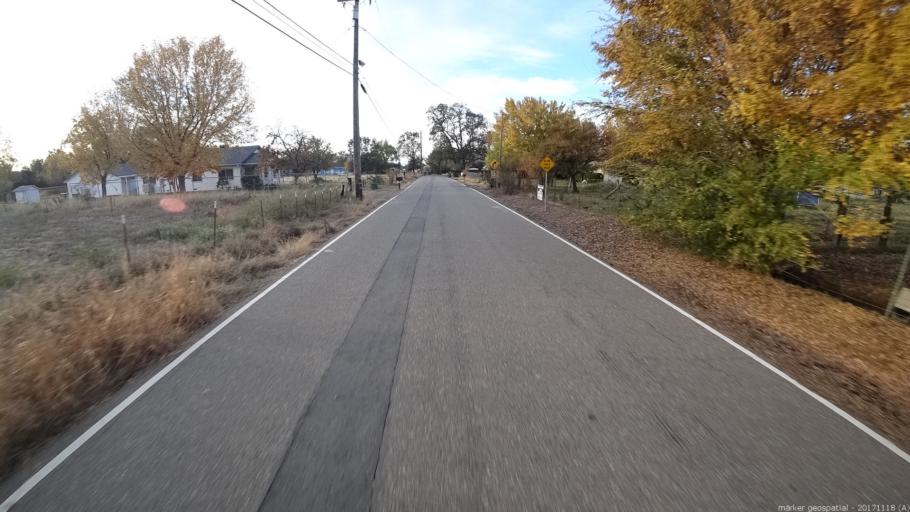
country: US
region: California
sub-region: Shasta County
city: Anderson
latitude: 40.4631
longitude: -122.3155
